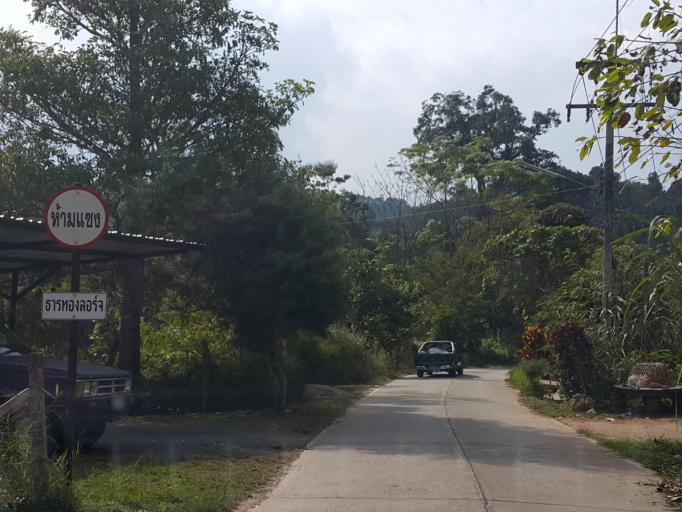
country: TH
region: Chiang Mai
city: Mae On
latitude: 18.8681
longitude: 99.3280
